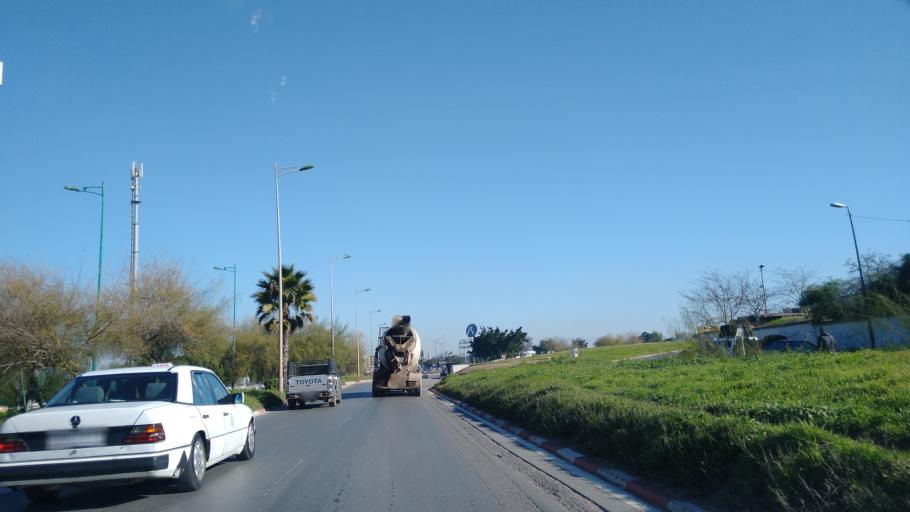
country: MA
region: Rabat-Sale-Zemmour-Zaer
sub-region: Skhirate-Temara
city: Temara
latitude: 33.9455
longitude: -6.8731
